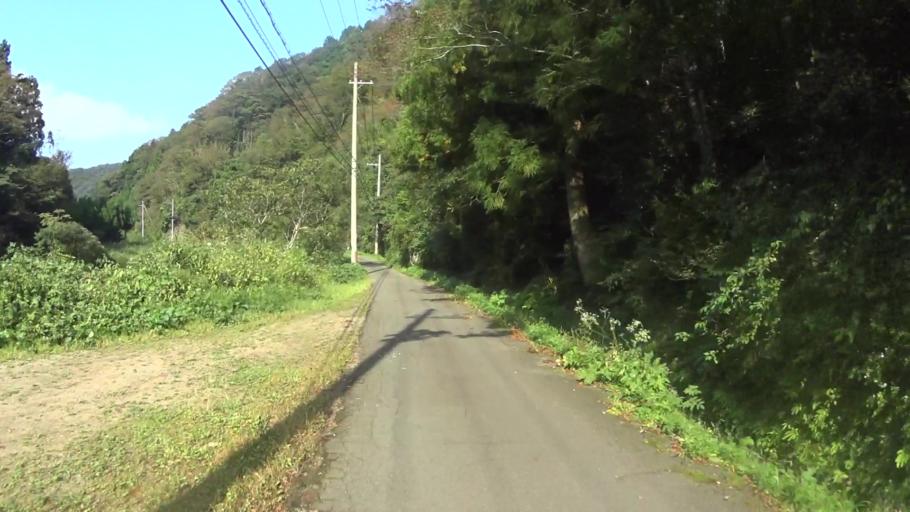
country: JP
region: Kyoto
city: Miyazu
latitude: 35.7240
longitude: 135.1622
